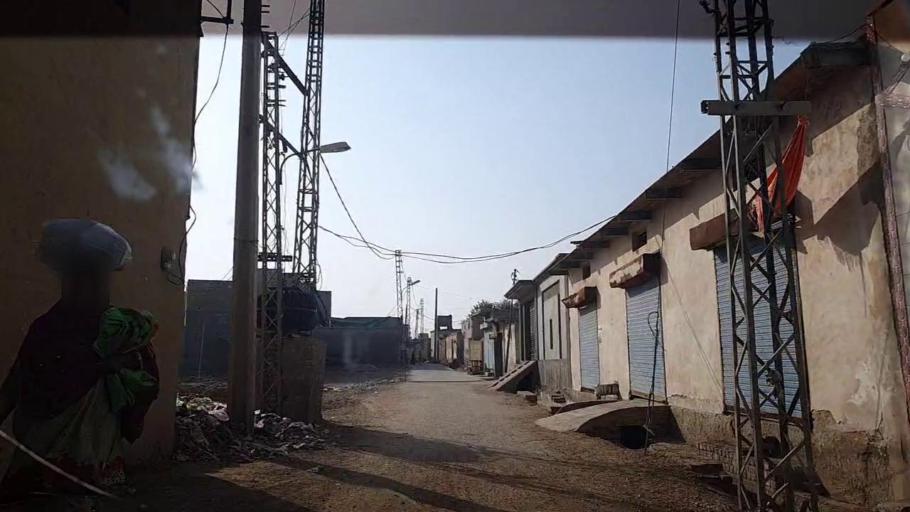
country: PK
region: Sindh
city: Shikarpur
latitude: 28.0702
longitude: 68.5966
